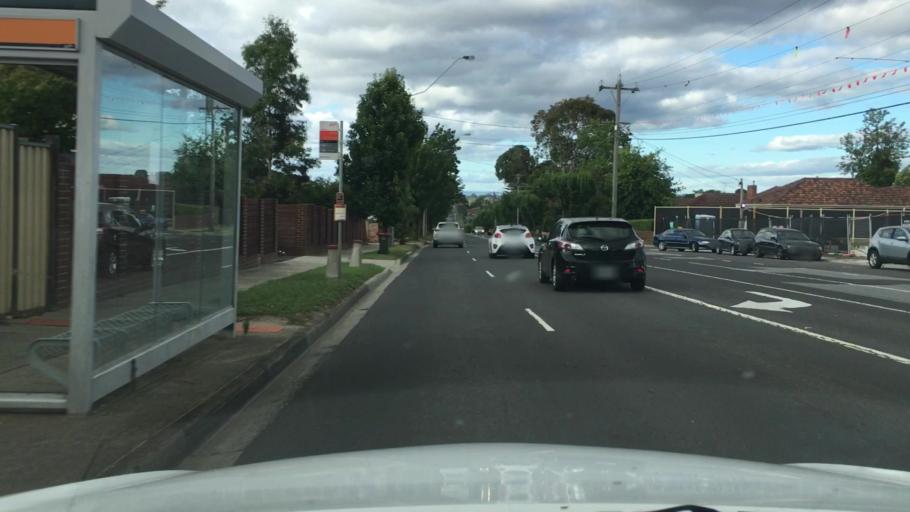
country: AU
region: Victoria
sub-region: Whitehorse
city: Burwood
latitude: -37.8456
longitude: 145.1335
